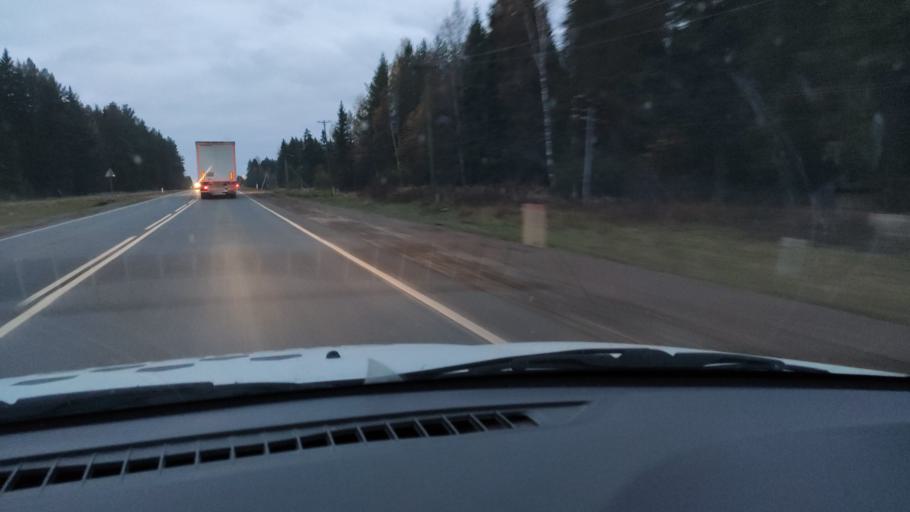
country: RU
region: Kirov
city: Kostino
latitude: 58.8411
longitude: 53.3023
